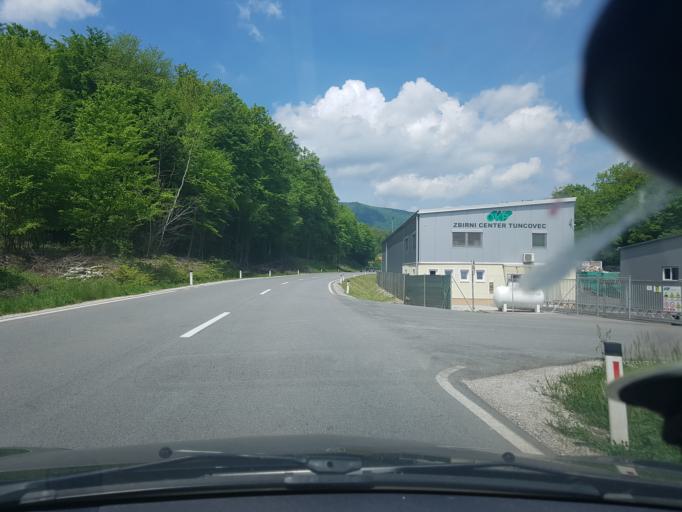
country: SI
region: Rogatec
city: Rogatec
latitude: 46.2355
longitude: 15.6718
